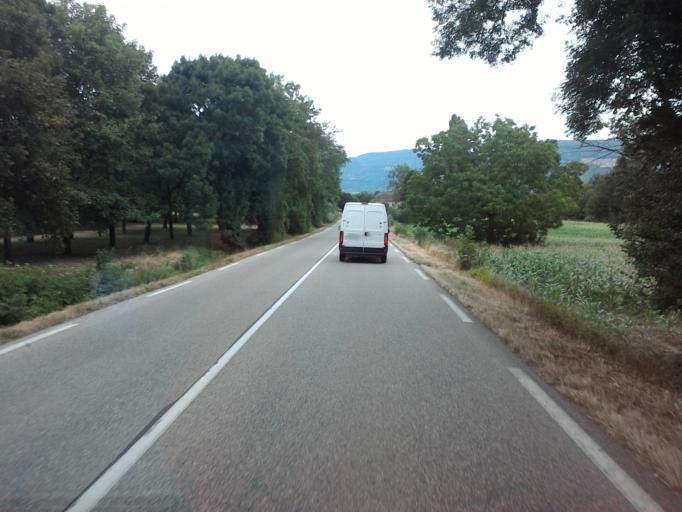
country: FR
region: Rhone-Alpes
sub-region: Departement de l'Isere
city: Bouvesse-Quirieu
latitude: 45.7922
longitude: 5.4019
